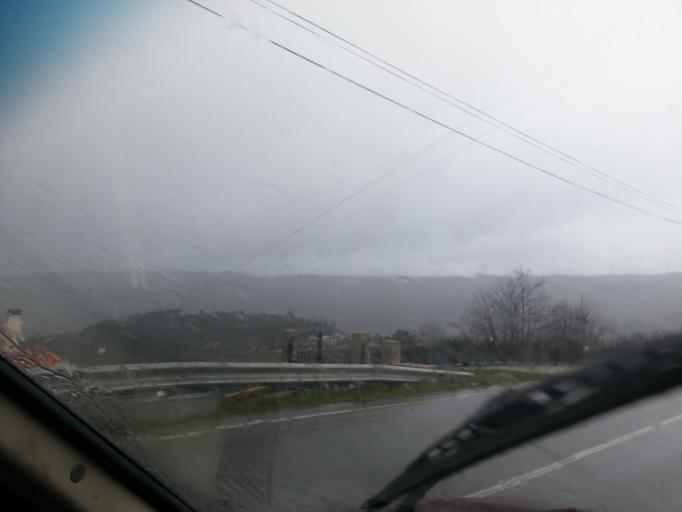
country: PT
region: Guarda
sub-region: Guarda
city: Guarda
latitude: 40.5418
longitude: -7.3163
